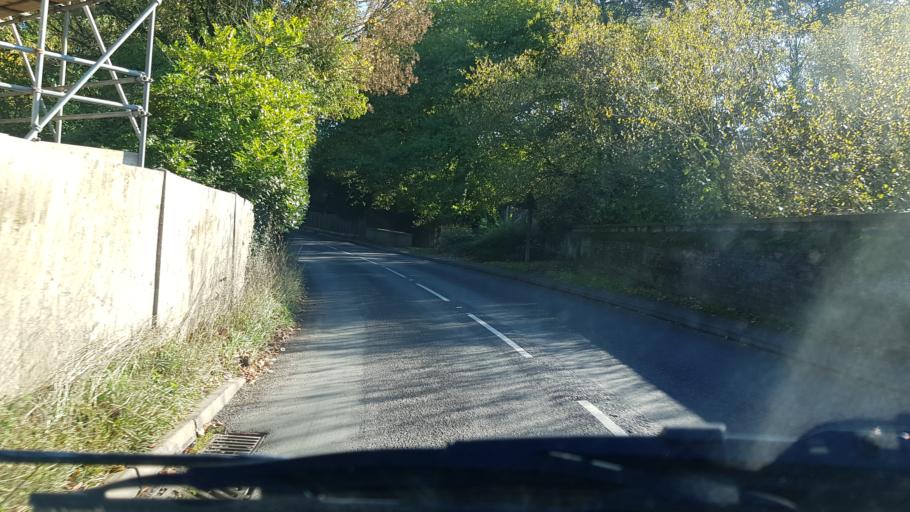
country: GB
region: England
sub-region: Surrey
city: Chilworth
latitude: 51.2201
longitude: -0.5018
